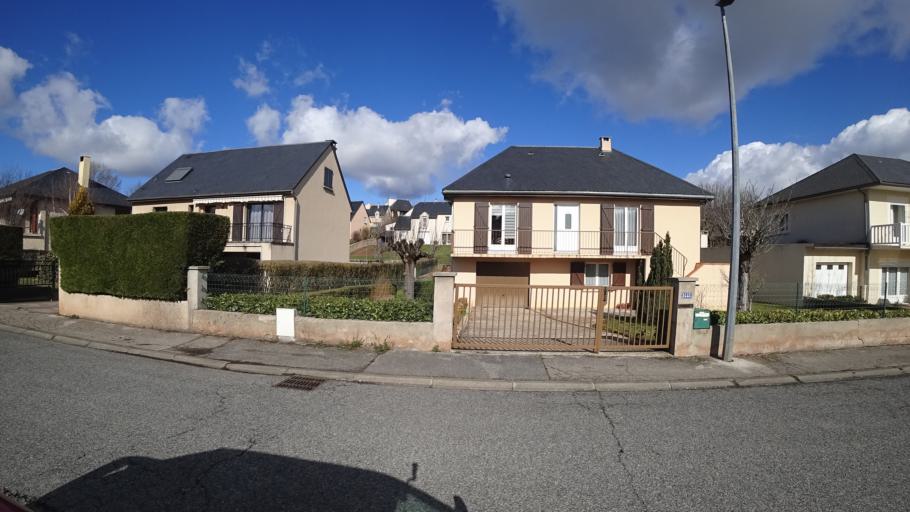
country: FR
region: Midi-Pyrenees
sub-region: Departement de l'Aveyron
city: Rodez
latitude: 44.3662
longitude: 2.5597
